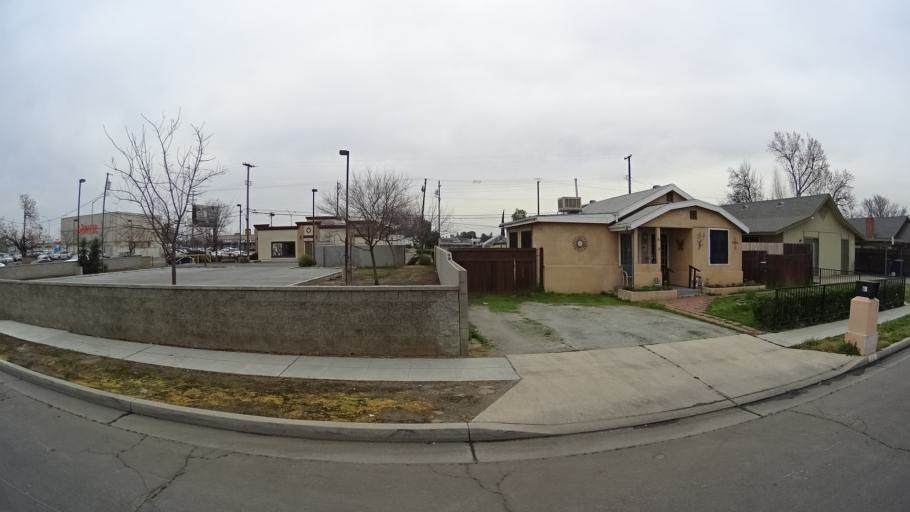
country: US
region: California
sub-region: Fresno County
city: Clovis
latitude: 36.8383
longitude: -119.7915
